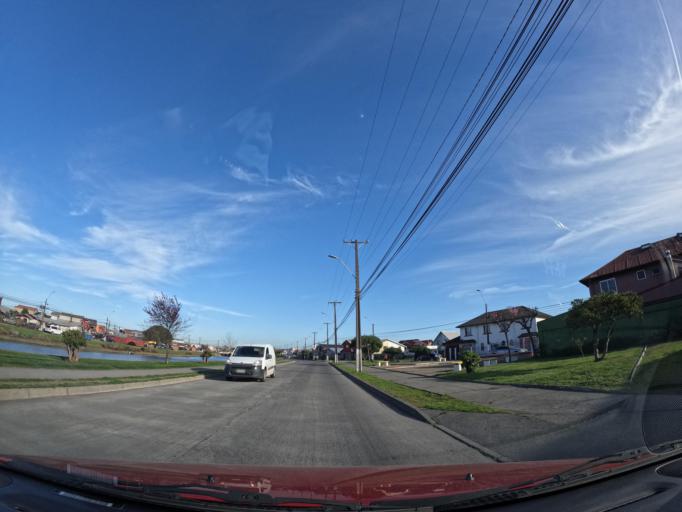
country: CL
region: Biobio
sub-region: Provincia de Concepcion
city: Talcahuano
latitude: -36.7522
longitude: -73.0851
